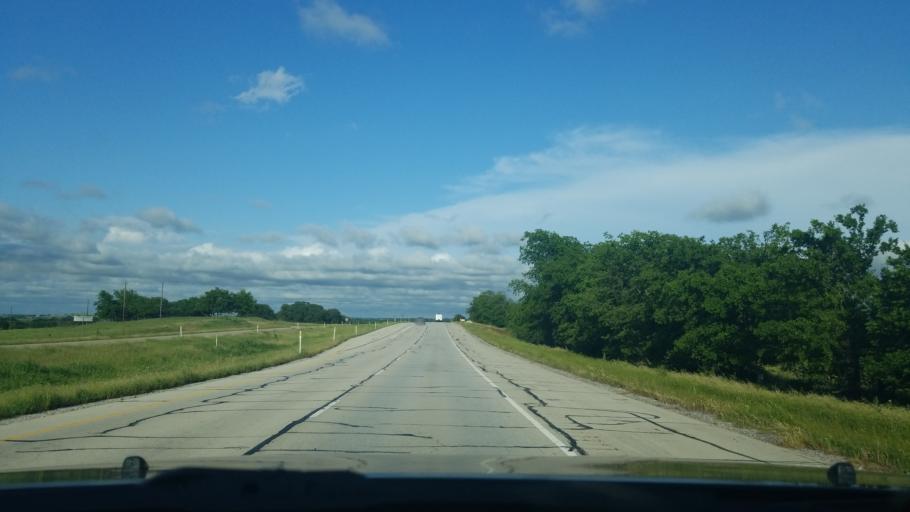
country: US
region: Texas
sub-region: Wise County
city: Decatur
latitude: 33.2449
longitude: -97.4819
